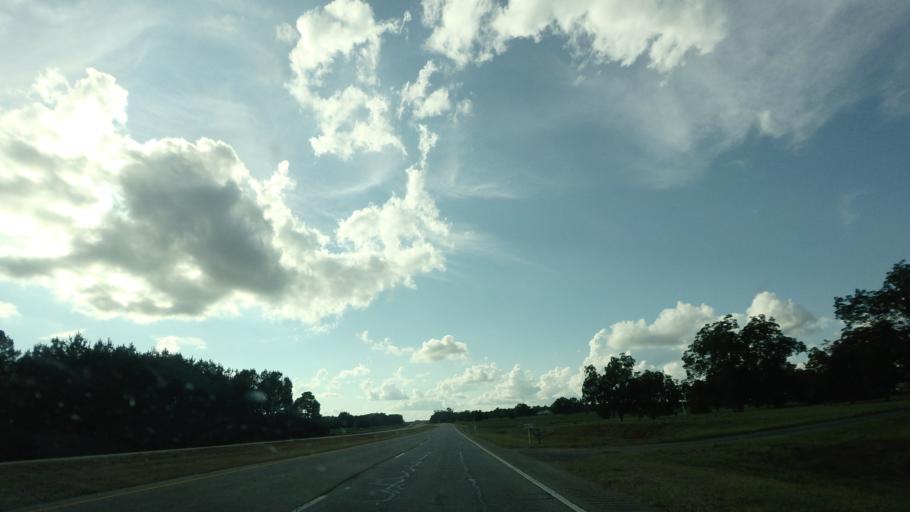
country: US
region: Georgia
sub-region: Pulaski County
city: Hawkinsville
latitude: 32.3123
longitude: -83.5204
